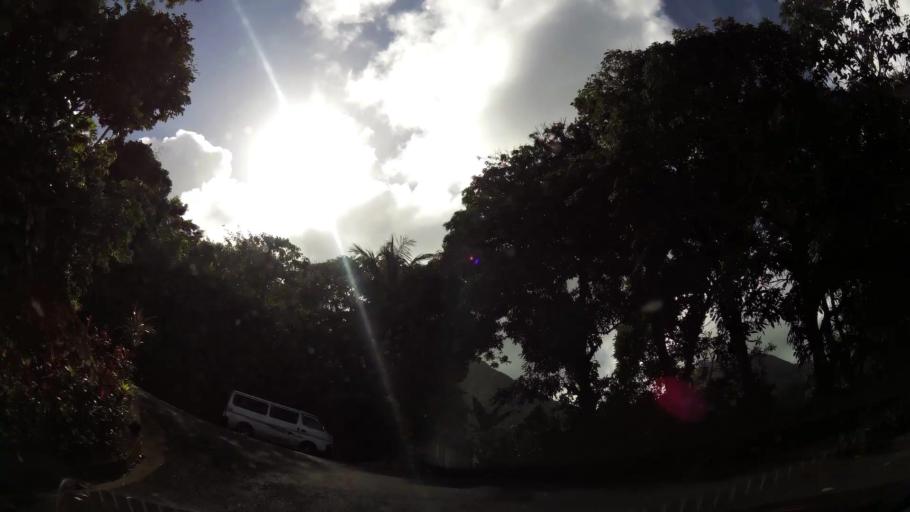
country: DM
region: Saint Andrew
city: Calibishie
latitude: 15.6097
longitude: -61.4042
